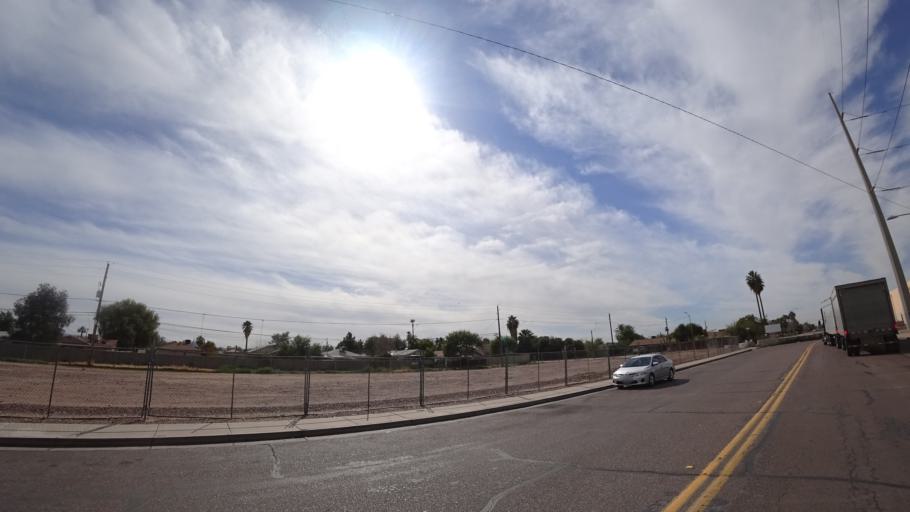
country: US
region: Arizona
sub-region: Maricopa County
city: Phoenix
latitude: 33.4732
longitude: -112.1249
